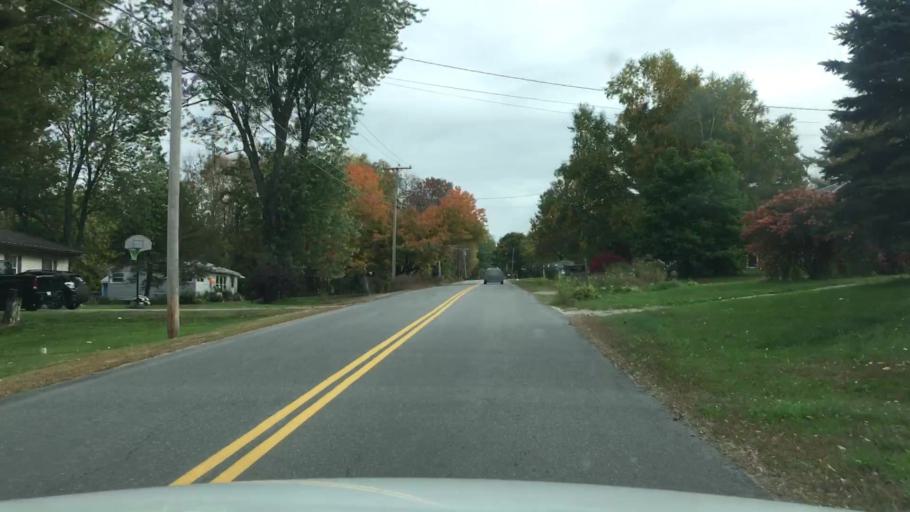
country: US
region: Maine
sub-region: Kennebec County
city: Waterville
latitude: 44.5664
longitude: -69.6751
